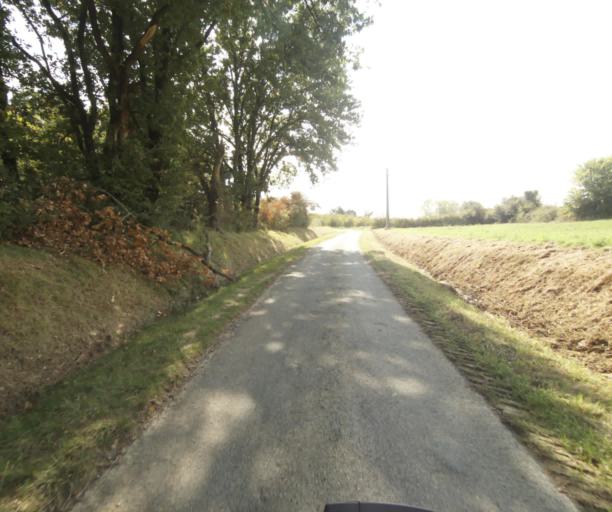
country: FR
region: Midi-Pyrenees
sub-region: Departement du Tarn-et-Garonne
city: Finhan
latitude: 43.8791
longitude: 1.1866
